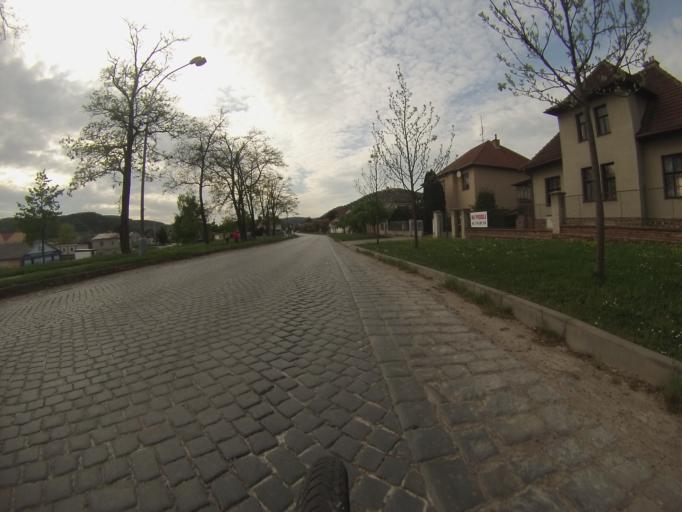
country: CZ
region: South Moravian
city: Tisnov
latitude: 49.3429
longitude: 16.4299
